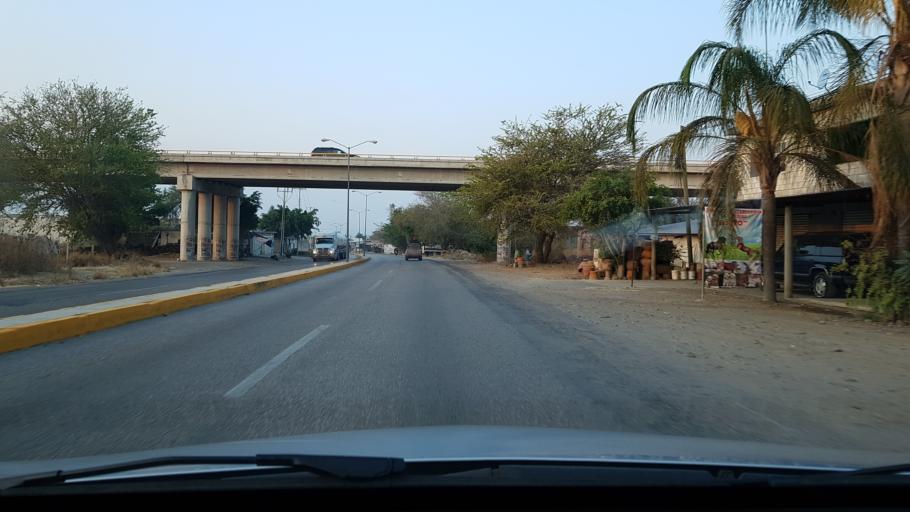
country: MX
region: Morelos
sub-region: Jonacatepec
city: Amacuitlapilco
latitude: 18.7070
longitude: -98.7998
